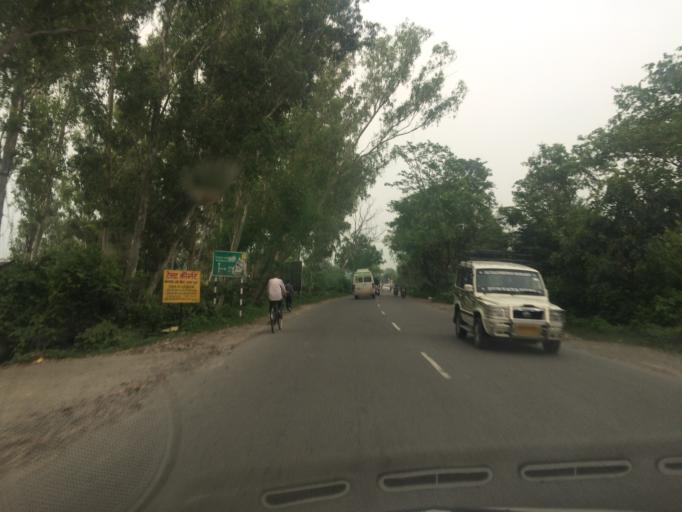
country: IN
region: Uttarakhand
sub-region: Dehradun
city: Doiwala
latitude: 30.1796
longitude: 78.1345
